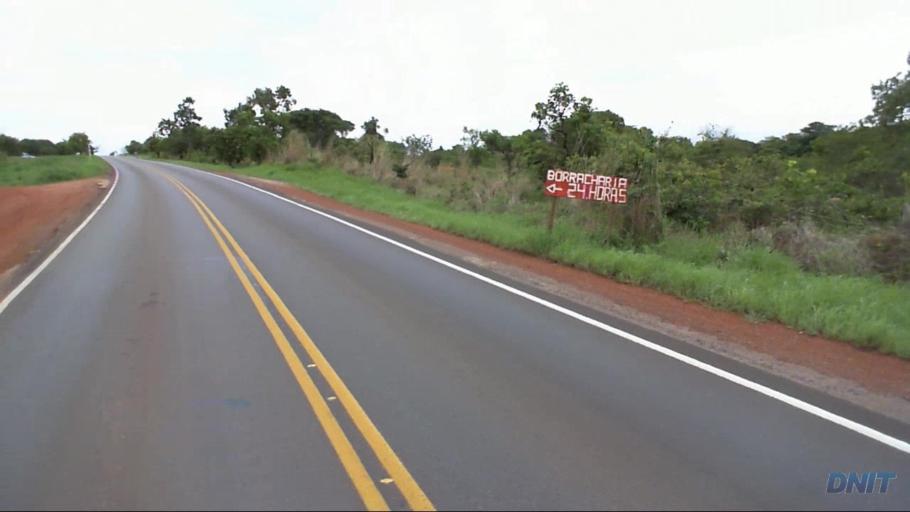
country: BR
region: Goias
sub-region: Padre Bernardo
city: Padre Bernardo
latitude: -15.3929
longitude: -48.2023
